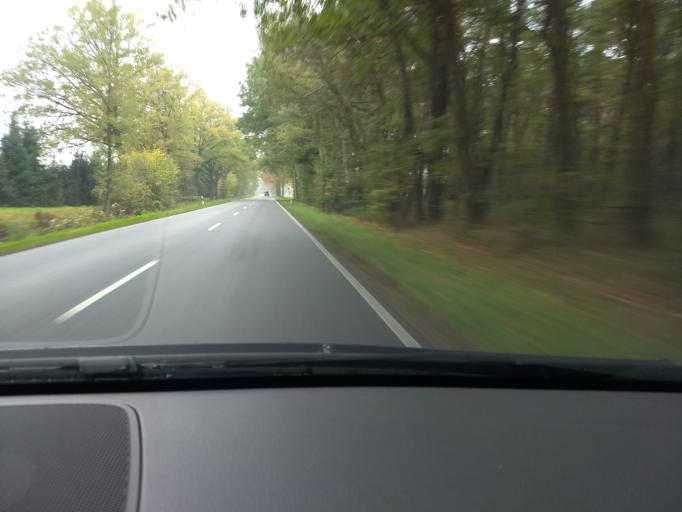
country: DE
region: North Rhine-Westphalia
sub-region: Regierungsbezirk Munster
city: Sudlohn
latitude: 51.9584
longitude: 6.8404
